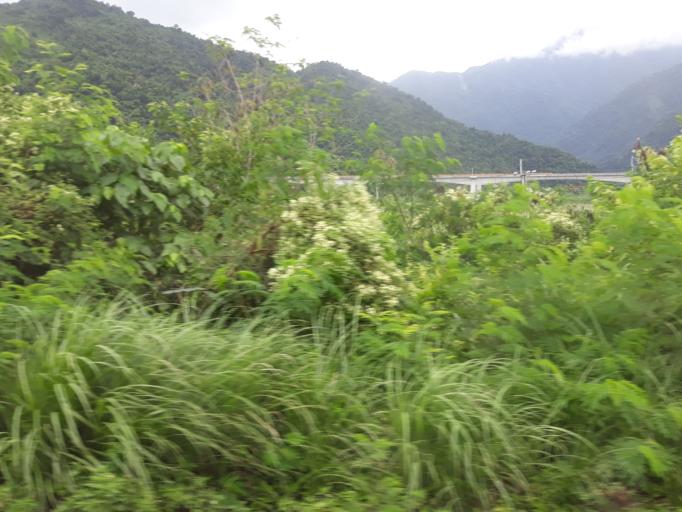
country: TW
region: Taiwan
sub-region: Yilan
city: Yilan
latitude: 24.4393
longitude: 121.7806
